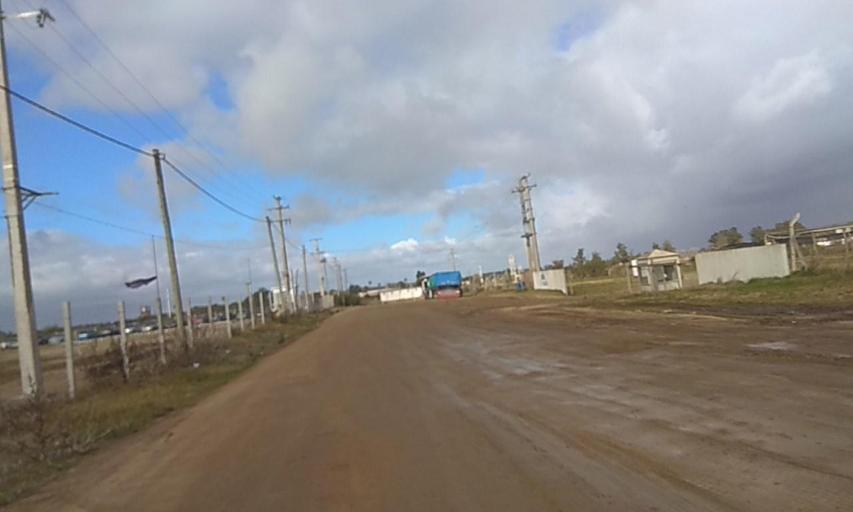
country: UY
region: Florida
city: Florida
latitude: -34.0913
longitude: -56.1886
